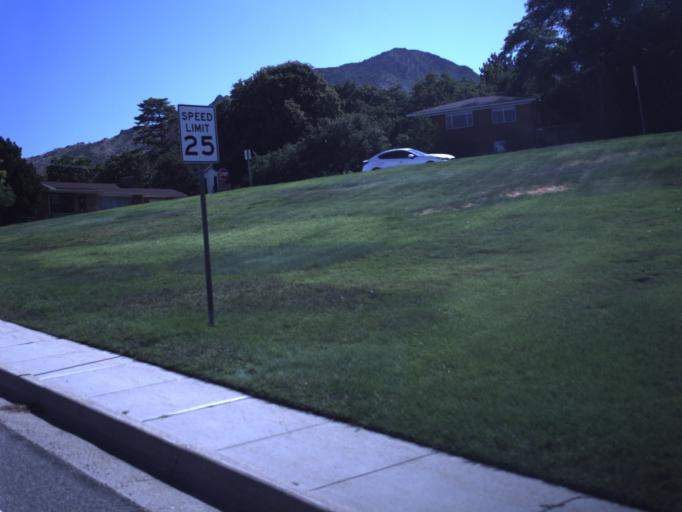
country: US
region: Utah
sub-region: Salt Lake County
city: Mount Olympus
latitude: 40.6742
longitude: -111.8008
